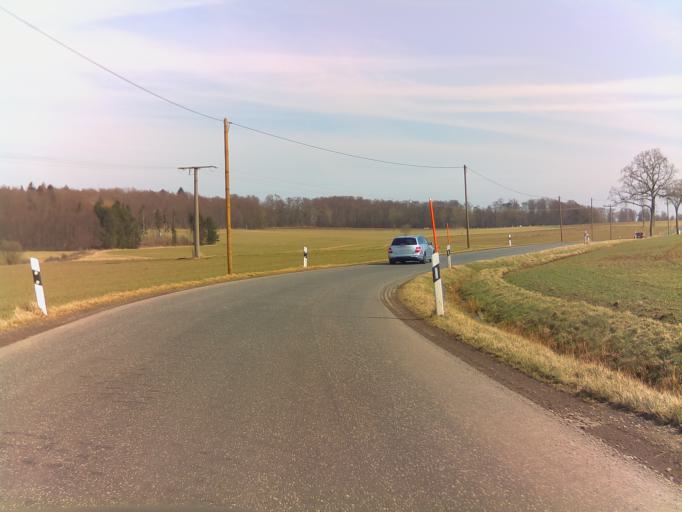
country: DE
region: Hesse
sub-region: Regierungsbezirk Giessen
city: Schwalmtal
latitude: 50.6554
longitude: 9.2046
